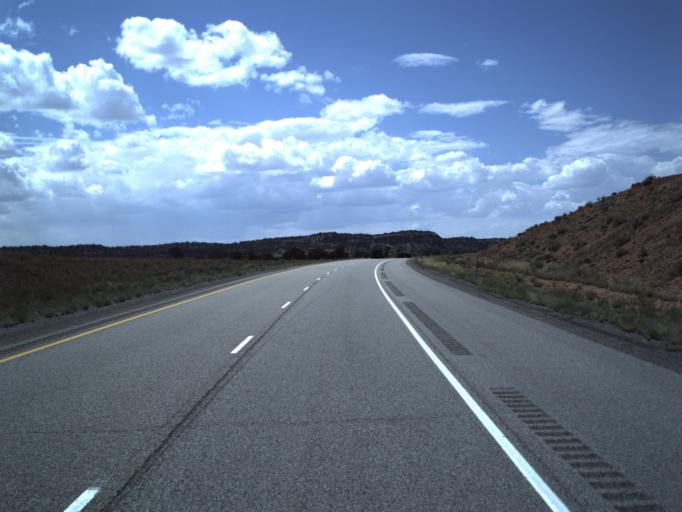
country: US
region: Utah
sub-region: Emery County
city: Castle Dale
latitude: 38.8674
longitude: -110.7112
